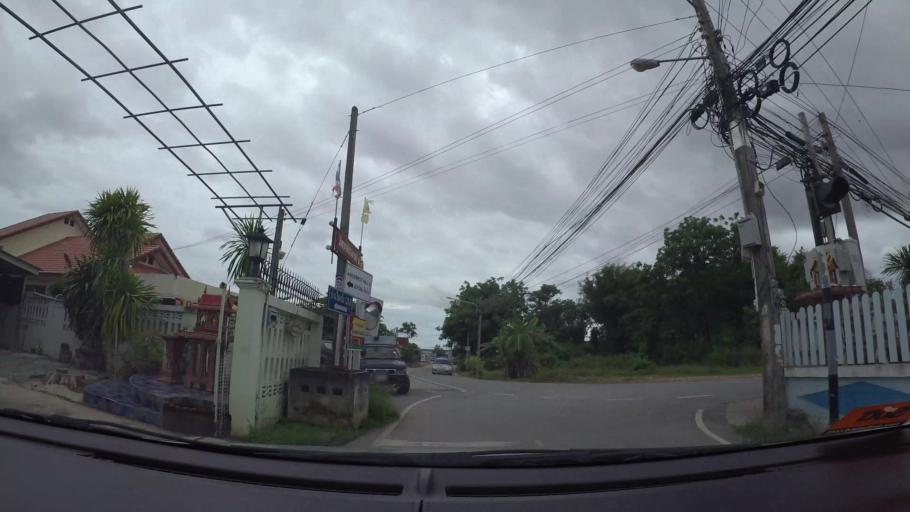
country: TH
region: Chon Buri
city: Sattahip
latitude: 12.7241
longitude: 100.9021
